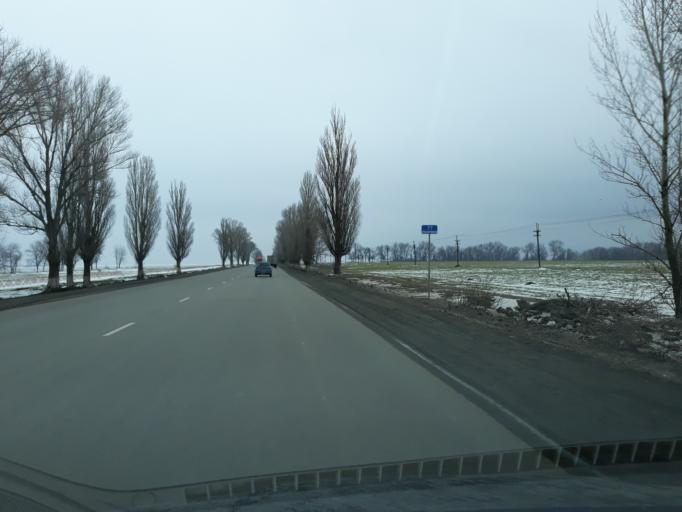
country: RU
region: Rostov
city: Primorka
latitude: 47.3059
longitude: 39.1490
